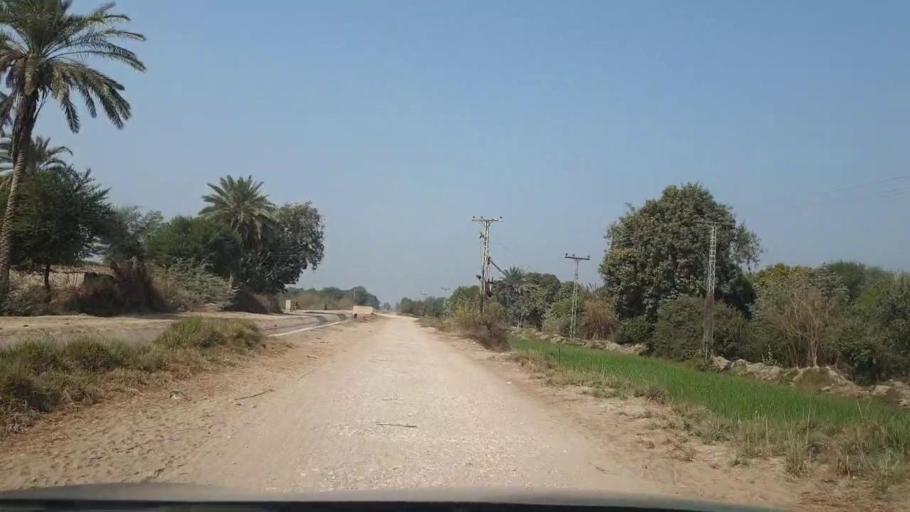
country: PK
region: Sindh
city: Tando Allahyar
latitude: 25.5271
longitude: 68.7501
